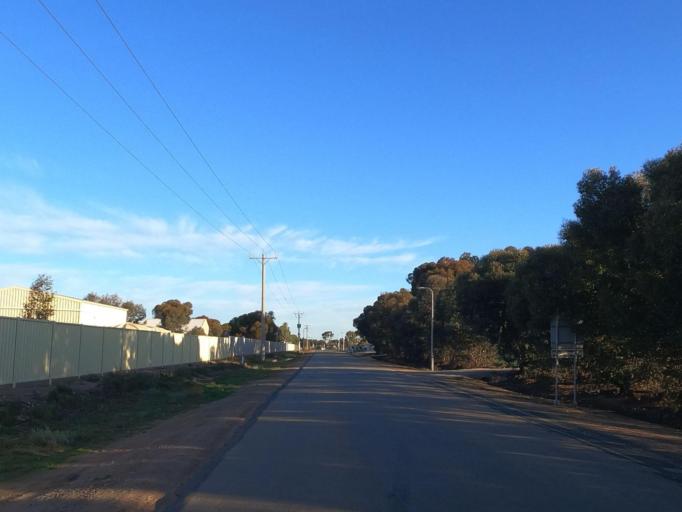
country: AU
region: Victoria
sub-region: Swan Hill
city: Swan Hill
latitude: -35.3303
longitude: 143.5346
